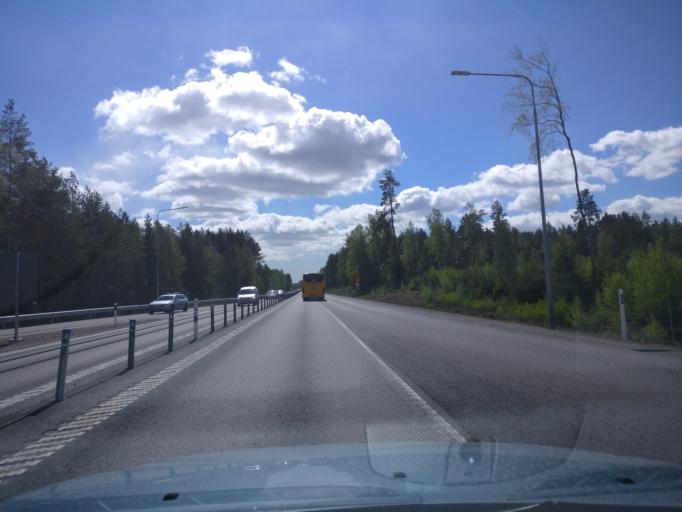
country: SE
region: Vaermland
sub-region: Karlstads Kommun
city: Karlstad
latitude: 59.4176
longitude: 13.5327
